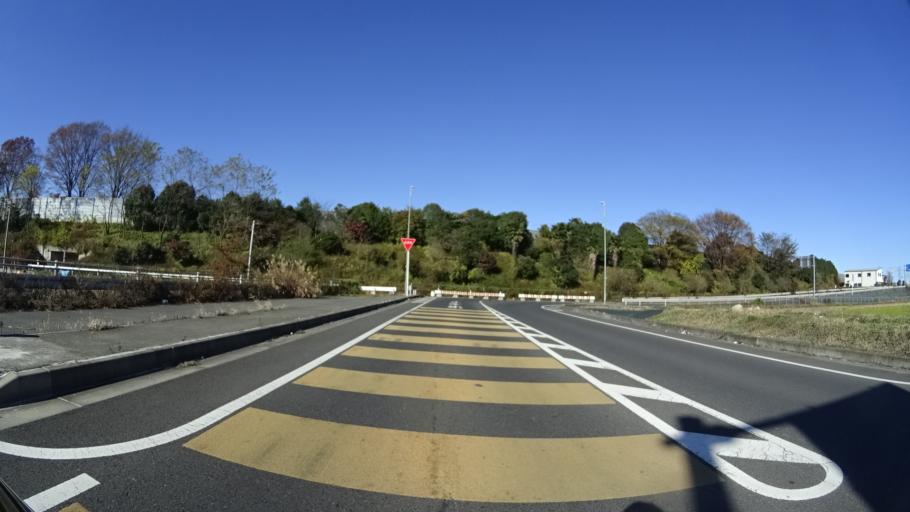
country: JP
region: Tochigi
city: Kanuma
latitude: 36.4958
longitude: 139.7520
